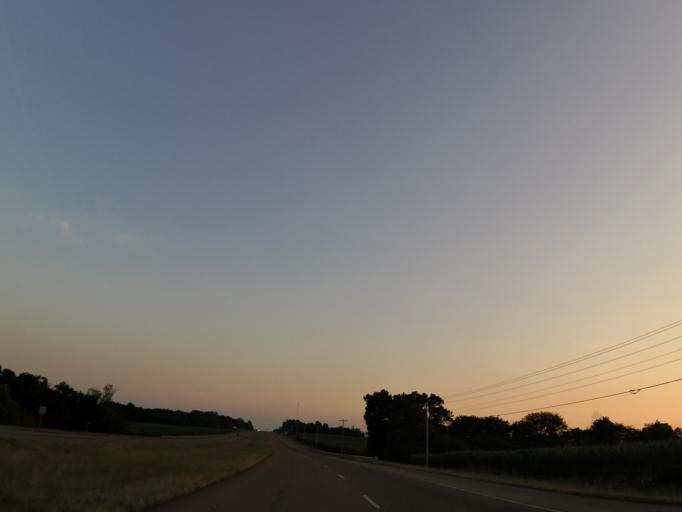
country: US
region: Tennessee
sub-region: Carroll County
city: McKenzie
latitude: 36.1945
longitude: -88.4260
